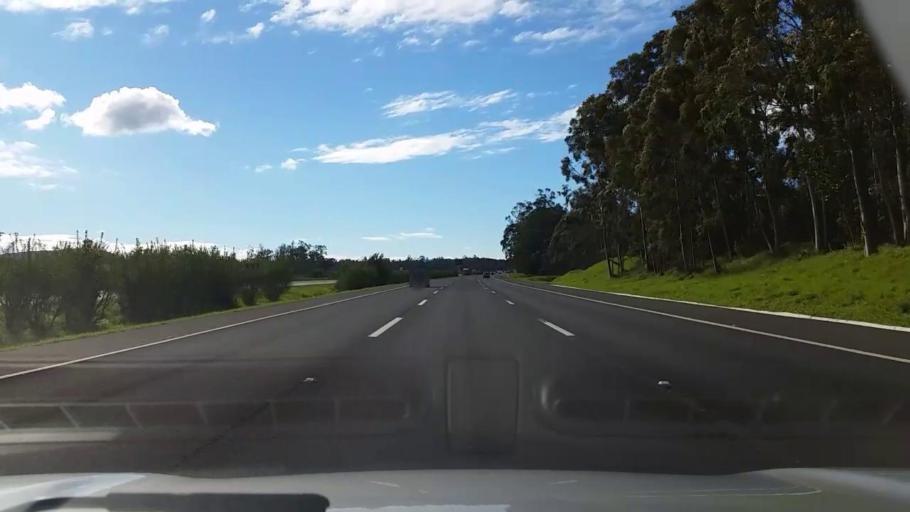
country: BR
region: Rio Grande do Sul
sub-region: Osorio
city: Osorio
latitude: -29.8797
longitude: -50.5072
